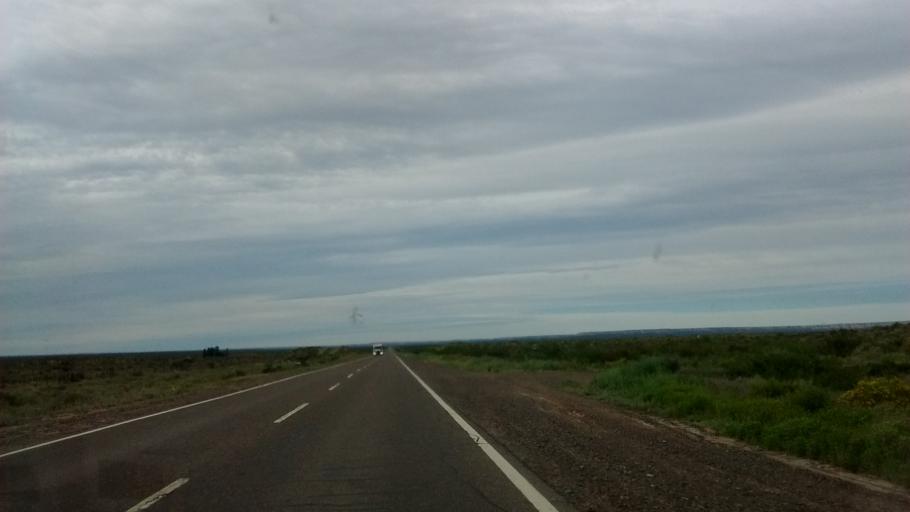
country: AR
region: Rio Negro
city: Catriel
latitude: -38.0360
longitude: -67.9173
